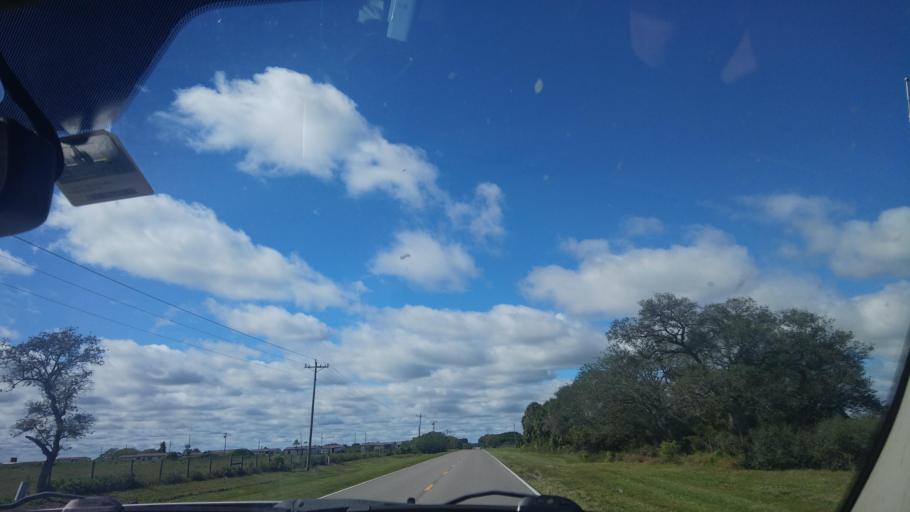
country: US
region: Florida
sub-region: Okeechobee County
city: Cypress Quarters
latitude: 27.3904
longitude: -80.8228
